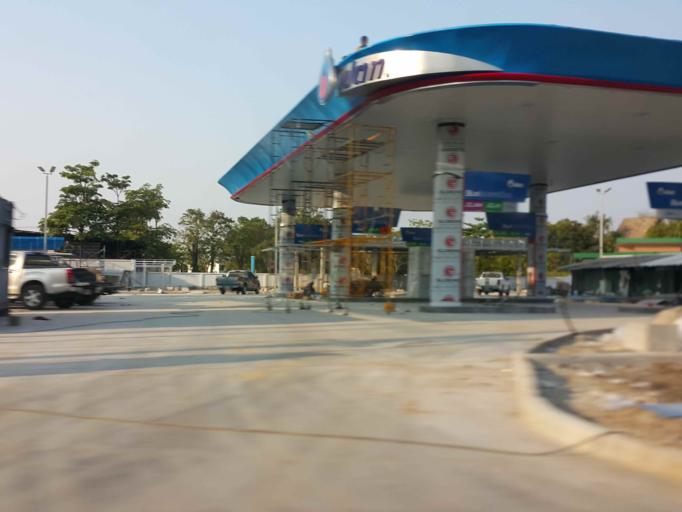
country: TH
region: Chiang Mai
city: Chiang Mai
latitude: 18.7717
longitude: 98.9720
